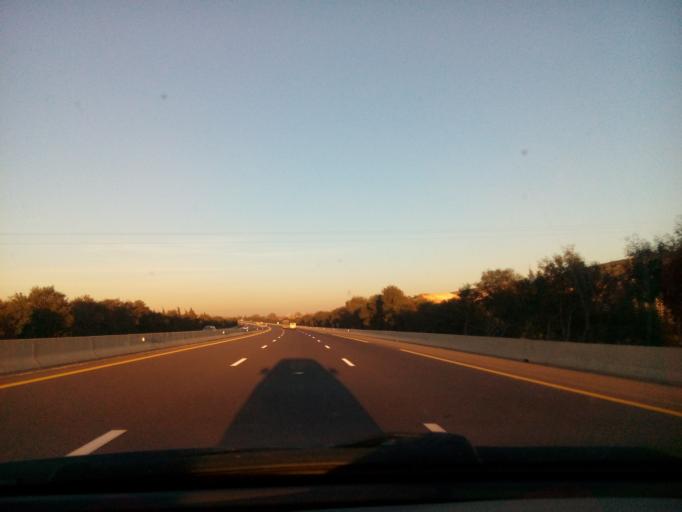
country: DZ
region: Relizane
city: Oued Rhiou
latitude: 36.0072
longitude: 1.0120
